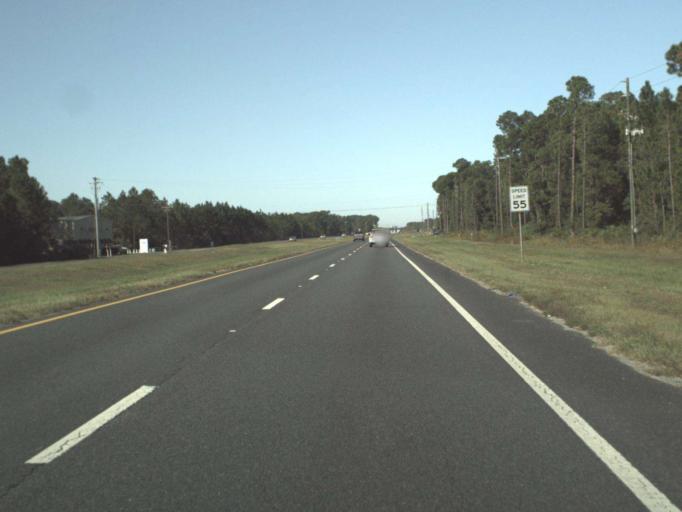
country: US
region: Florida
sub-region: Walton County
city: Miramar Beach
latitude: 30.3748
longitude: -86.2636
